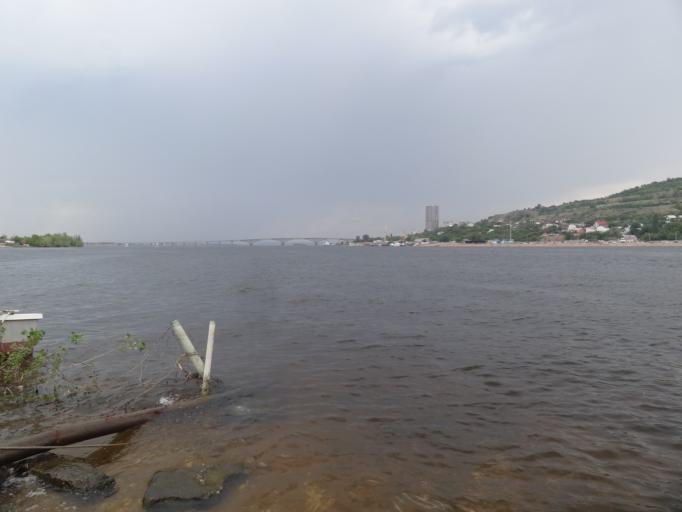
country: RU
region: Saratov
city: Engel's
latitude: 51.5388
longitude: 46.0855
